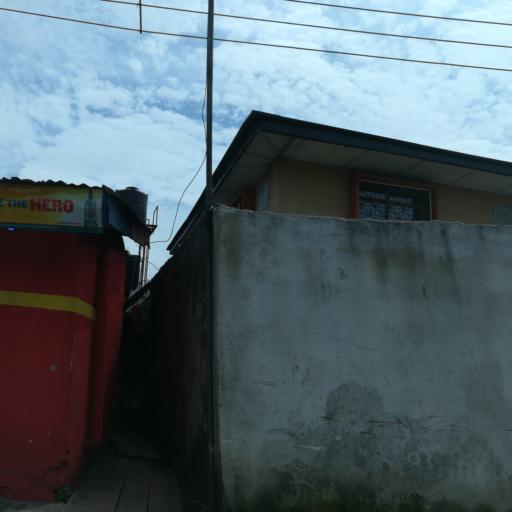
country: NG
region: Rivers
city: Port Harcourt
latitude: 4.7940
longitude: 7.0271
